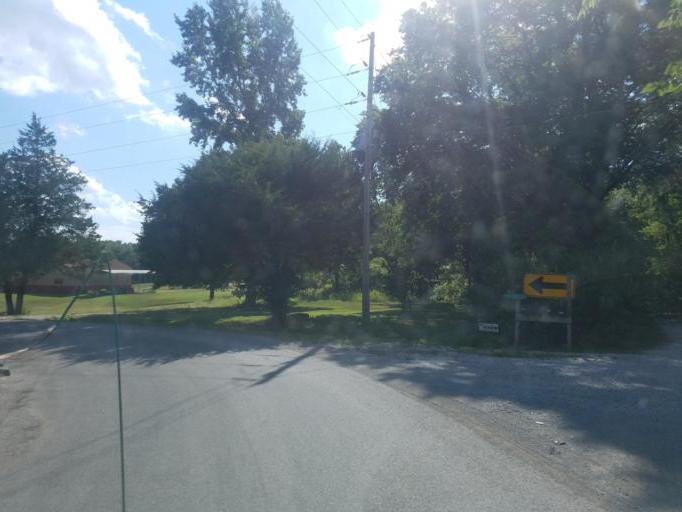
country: US
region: Illinois
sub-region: Jackson County
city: Murphysboro
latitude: 37.7164
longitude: -89.3003
